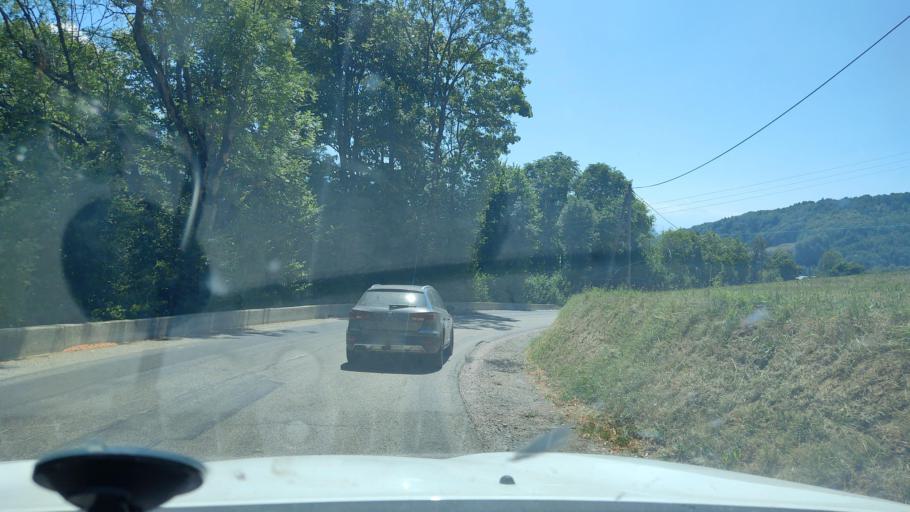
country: FR
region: Rhone-Alpes
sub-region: Departement de la Savoie
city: Barby
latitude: 45.6279
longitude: 6.0071
